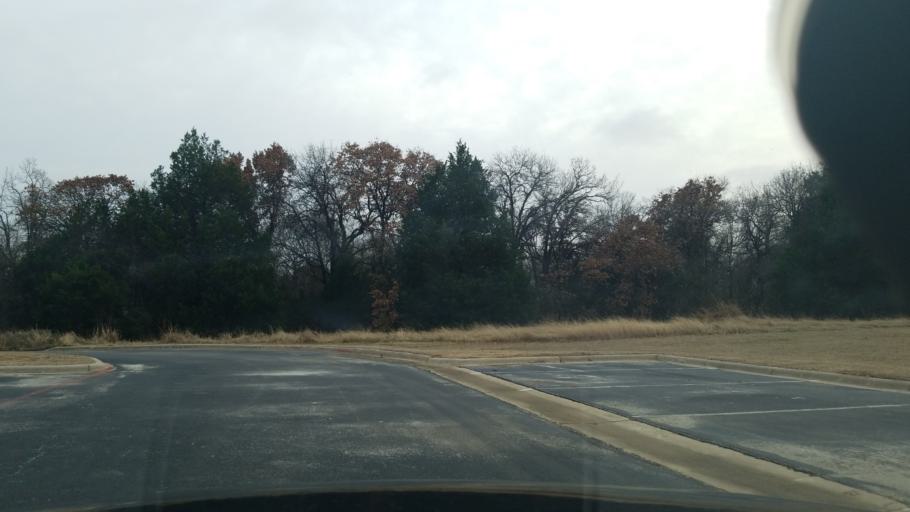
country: US
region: Texas
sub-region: Denton County
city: Corinth
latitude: 33.1513
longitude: -97.0507
